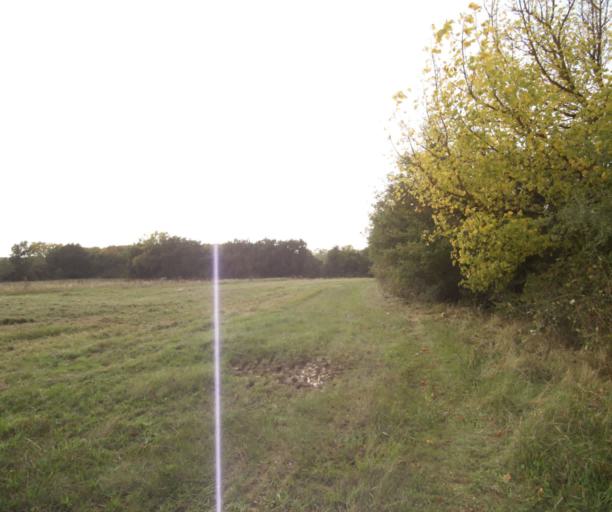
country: FR
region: Midi-Pyrenees
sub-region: Departement du Tarn-et-Garonne
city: Campsas
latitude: 43.9012
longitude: 1.3200
